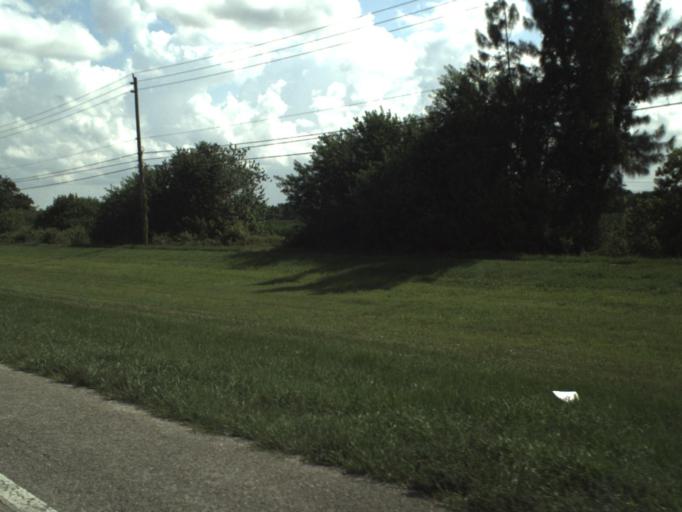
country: US
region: Florida
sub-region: Palm Beach County
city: Villages of Oriole
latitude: 26.4586
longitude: -80.2047
